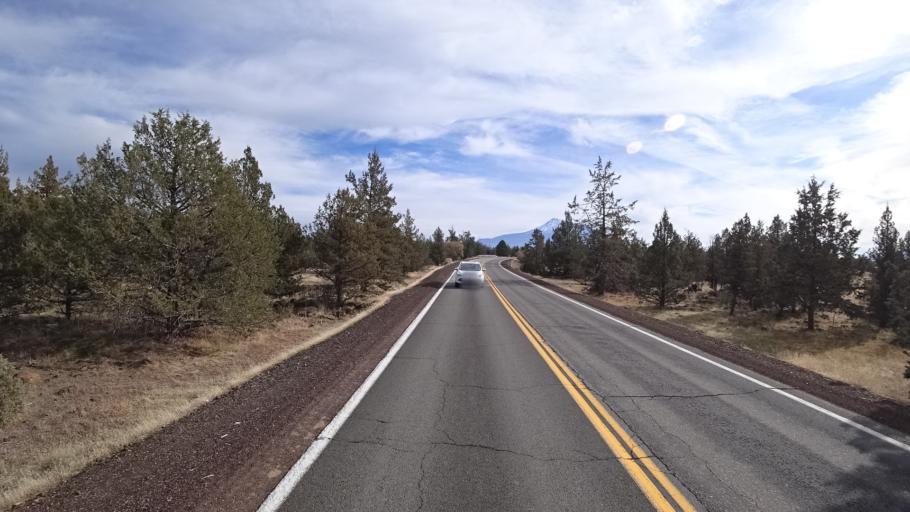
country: US
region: California
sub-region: Siskiyou County
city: Montague
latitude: 41.6070
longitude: -122.3964
